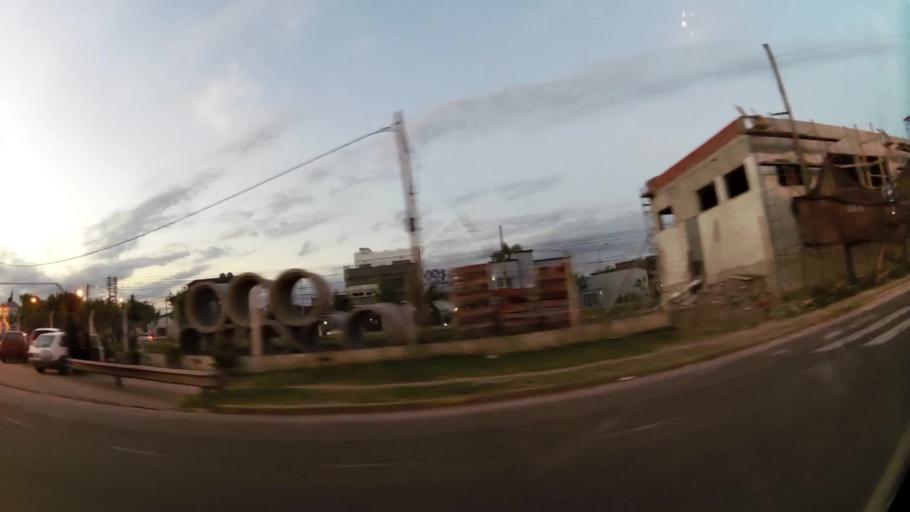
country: AR
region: Buenos Aires
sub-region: Partido de Merlo
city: Merlo
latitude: -34.6652
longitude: -58.6943
